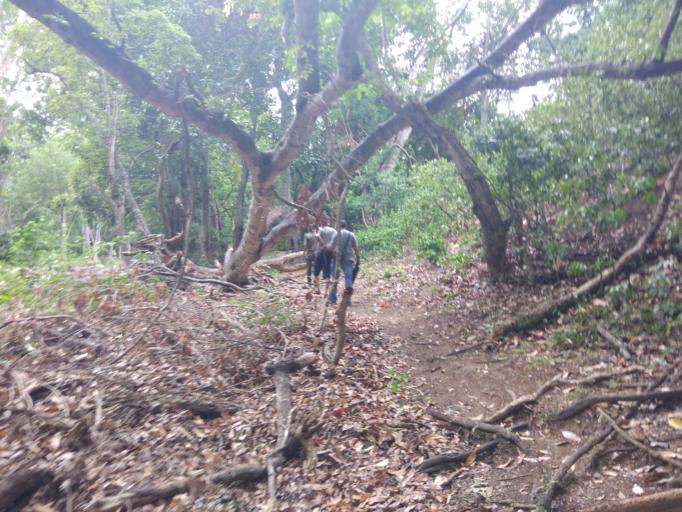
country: IN
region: Tamil Nadu
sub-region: Tiruppur
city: Dhali
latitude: 10.3535
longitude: 77.2238
